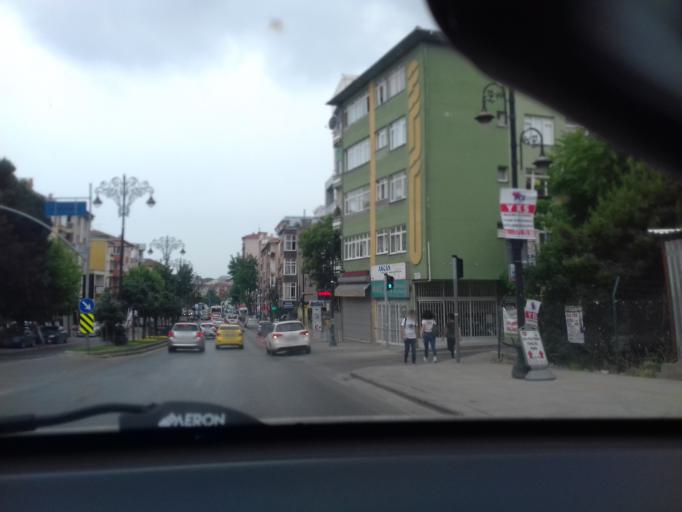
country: TR
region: Istanbul
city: Pendik
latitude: 40.8841
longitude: 29.2354
